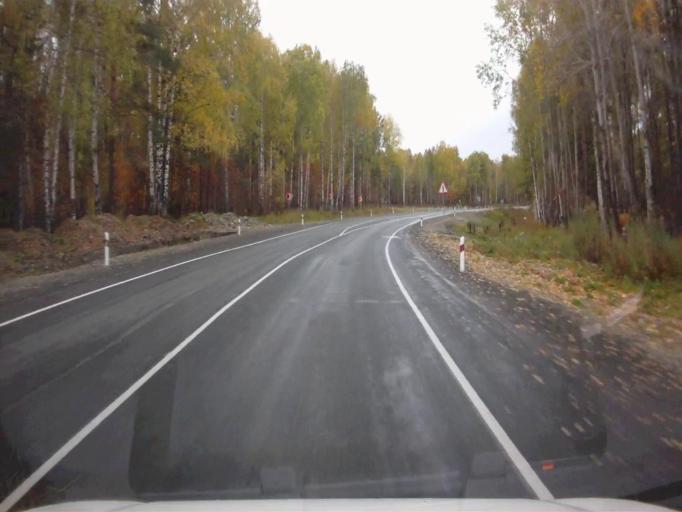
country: RU
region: Chelyabinsk
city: Nyazepetrovsk
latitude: 56.0602
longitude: 59.7311
